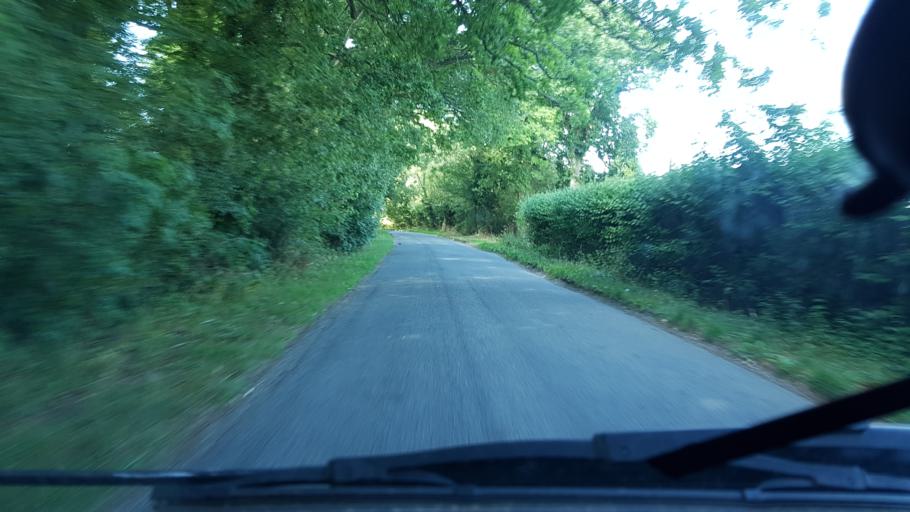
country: GB
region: England
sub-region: West Sussex
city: Horsham
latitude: 51.0963
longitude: -0.3531
